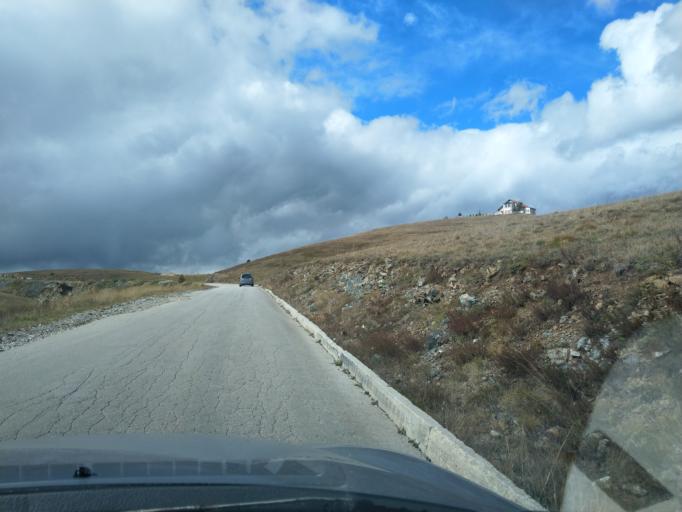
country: RS
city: Zlatibor
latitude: 43.7211
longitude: 19.7286
